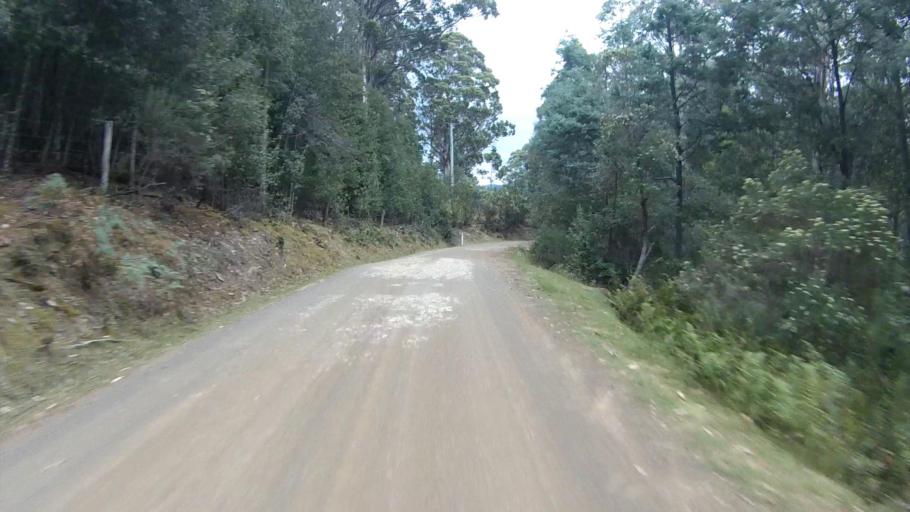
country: AU
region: Tasmania
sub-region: Huon Valley
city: Huonville
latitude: -42.9553
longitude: 147.0475
